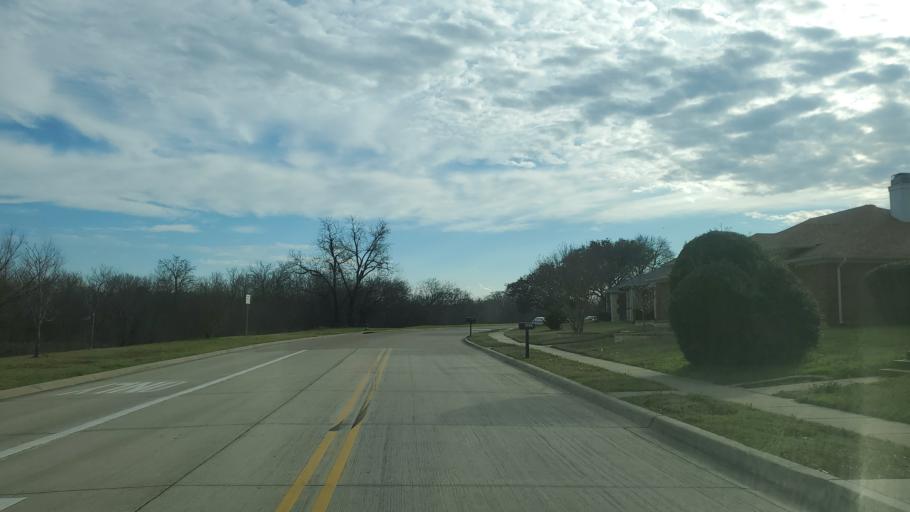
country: US
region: Texas
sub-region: Dallas County
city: Carrollton
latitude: 32.9987
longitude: -96.8939
